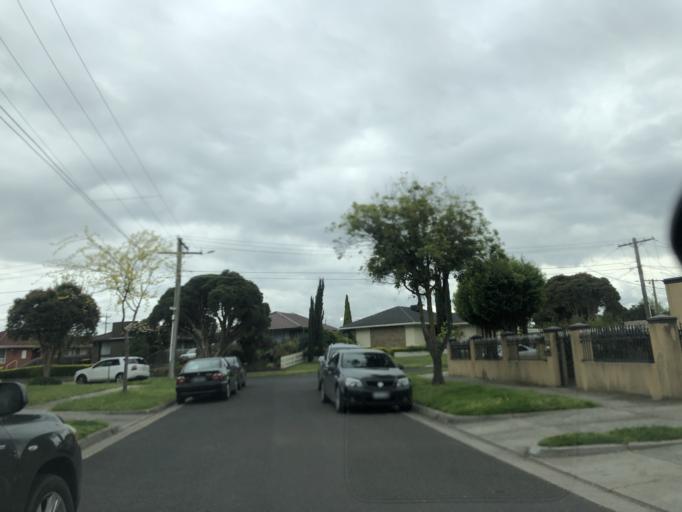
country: AU
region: Victoria
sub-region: Greater Dandenong
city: Dandenong
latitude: -37.9818
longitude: 145.1886
